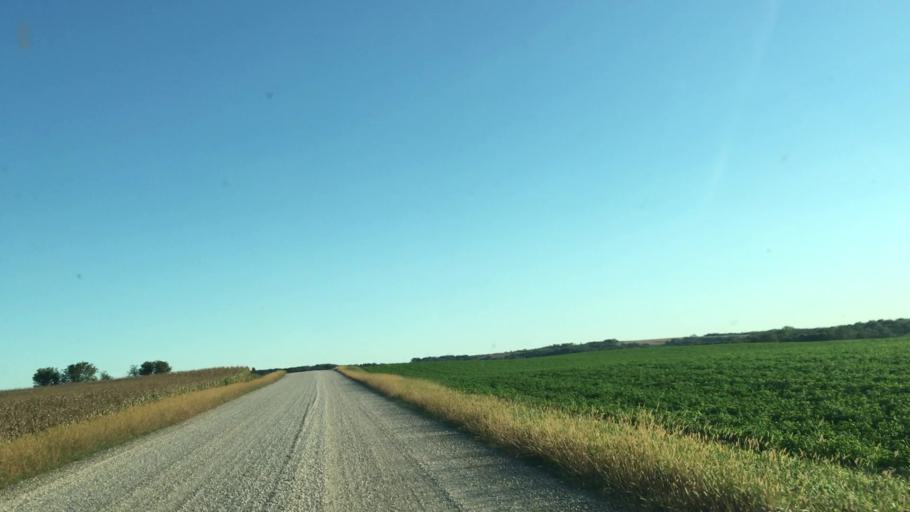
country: US
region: Minnesota
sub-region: Fillmore County
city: Preston
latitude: 43.7693
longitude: -92.0294
